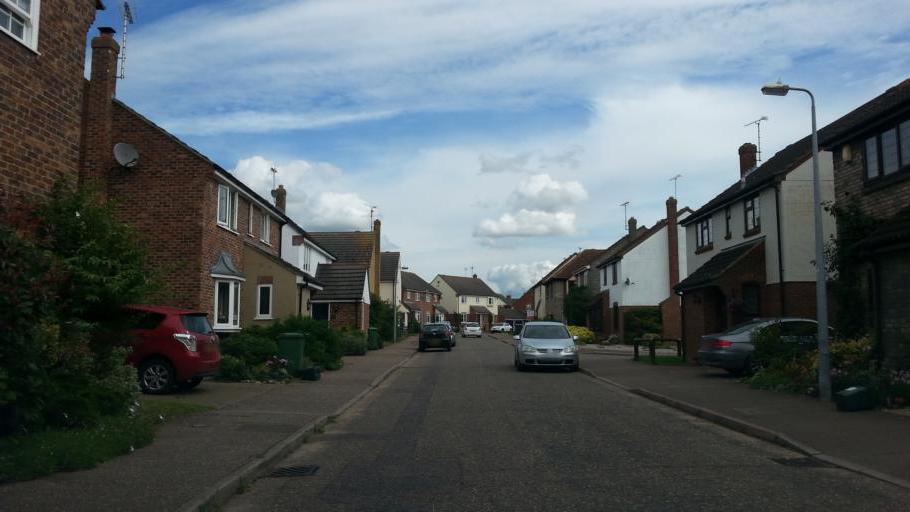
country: GB
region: England
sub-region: Essex
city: Kelvedon
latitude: 51.8342
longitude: 0.7029
